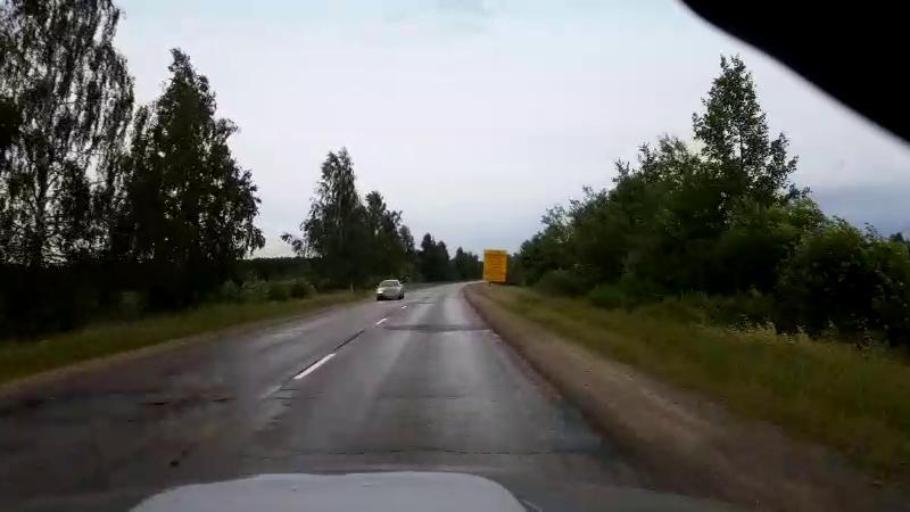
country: LV
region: Kekava
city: Kekava
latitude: 56.8091
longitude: 24.2712
